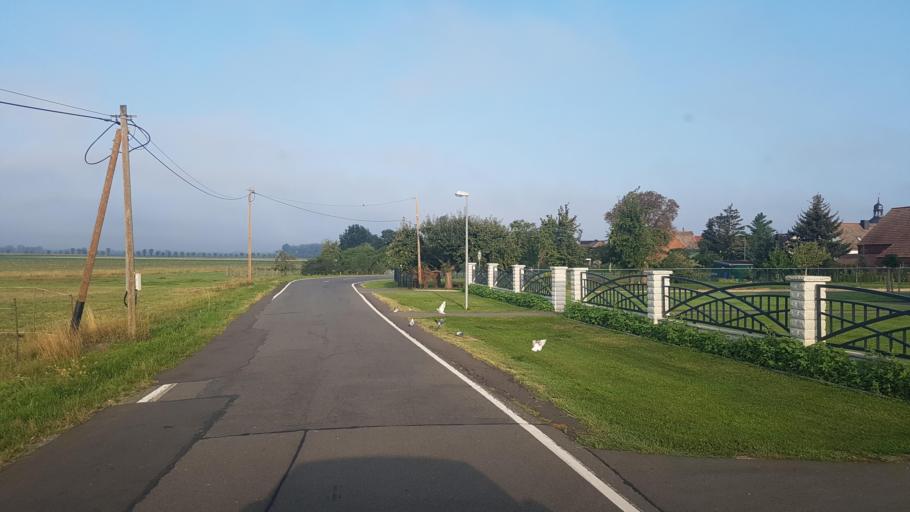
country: DE
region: Saxony
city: Dommitzsch
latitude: 51.7069
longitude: 12.8736
